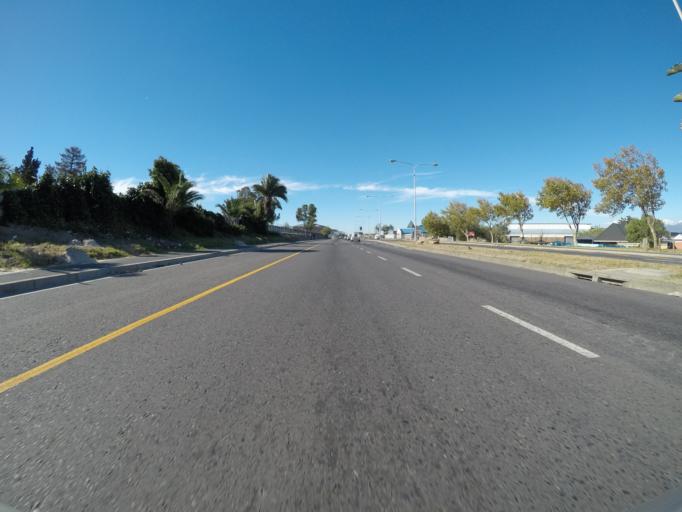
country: ZA
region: Western Cape
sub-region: City of Cape Town
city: Kraaifontein
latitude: -33.9087
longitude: 18.6662
